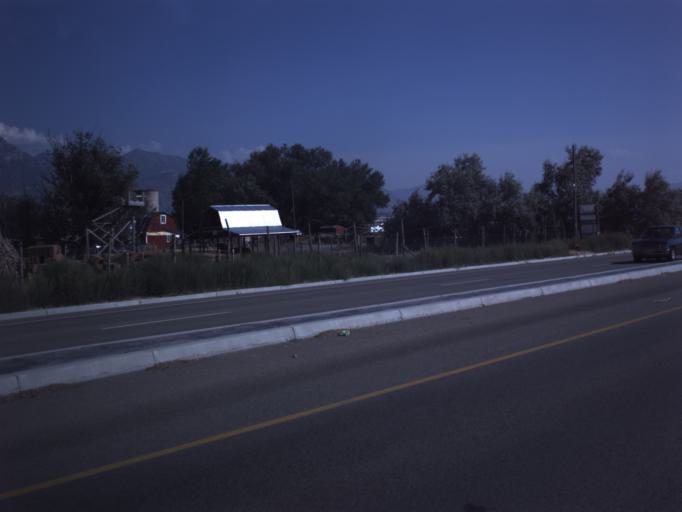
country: US
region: Utah
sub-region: Utah County
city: American Fork
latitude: 40.3624
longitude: -111.7691
